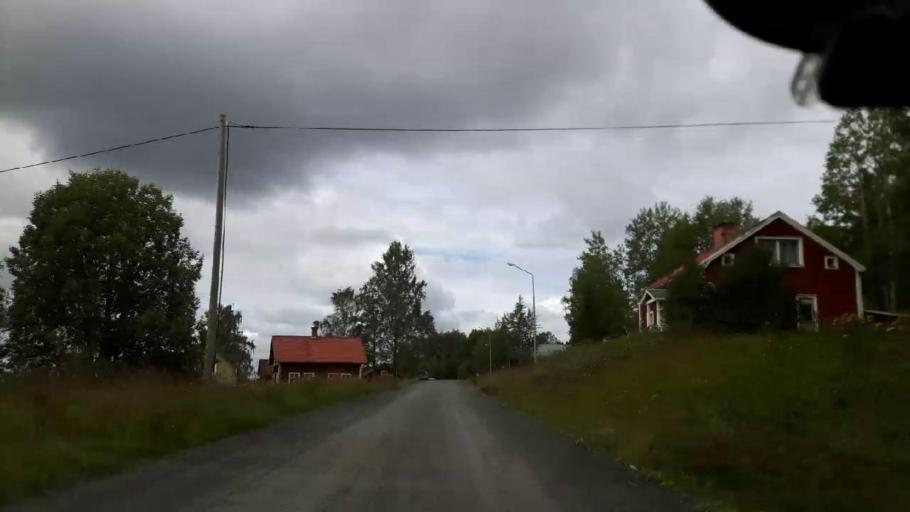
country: SE
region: Jaemtland
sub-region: Krokoms Kommun
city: Valla
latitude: 63.4914
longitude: 13.9836
